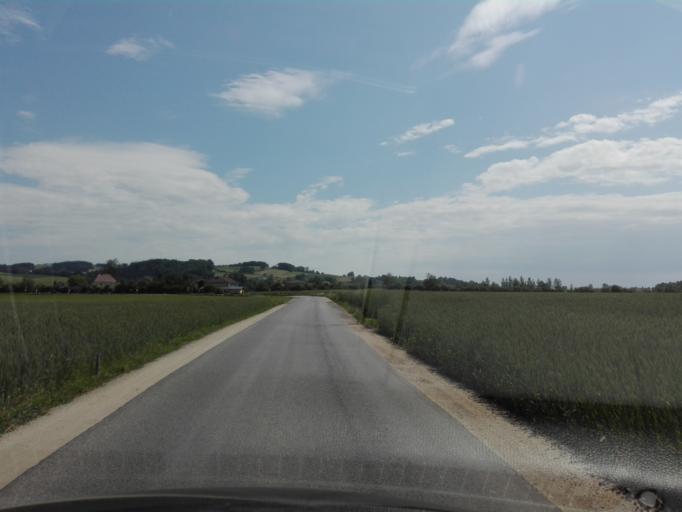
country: AT
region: Upper Austria
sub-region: Politischer Bezirk Perg
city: Perg
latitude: 48.2571
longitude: 14.5756
